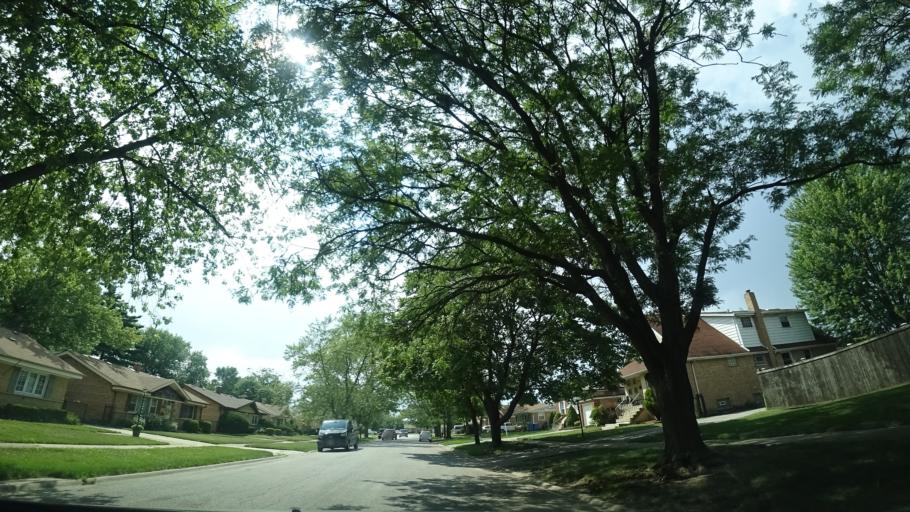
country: US
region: Illinois
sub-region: Cook County
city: Merrionette Park
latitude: 41.6741
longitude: -87.7125
